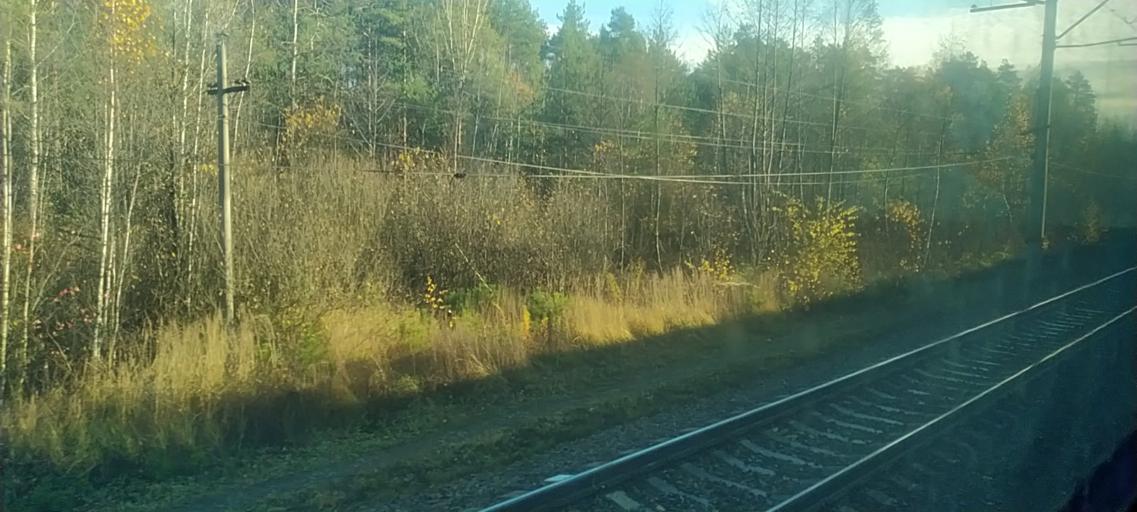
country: RU
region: Moskovskaya
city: Ramenskoye
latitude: 55.6387
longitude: 38.2602
